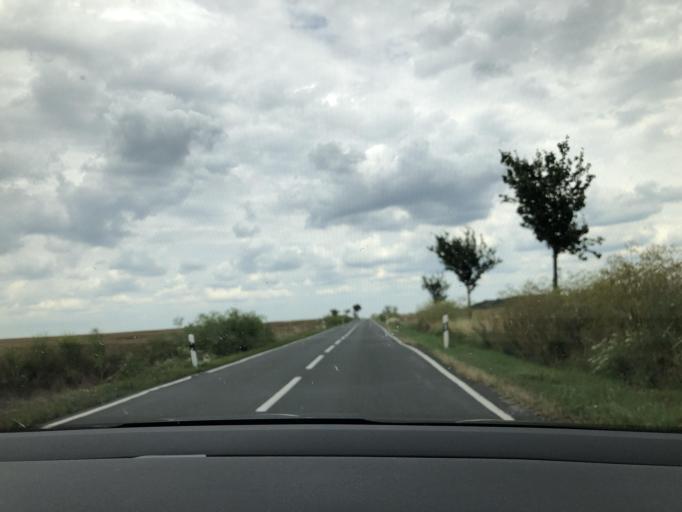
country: DE
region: Saxony-Anhalt
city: Biere
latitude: 51.9849
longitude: 11.6792
